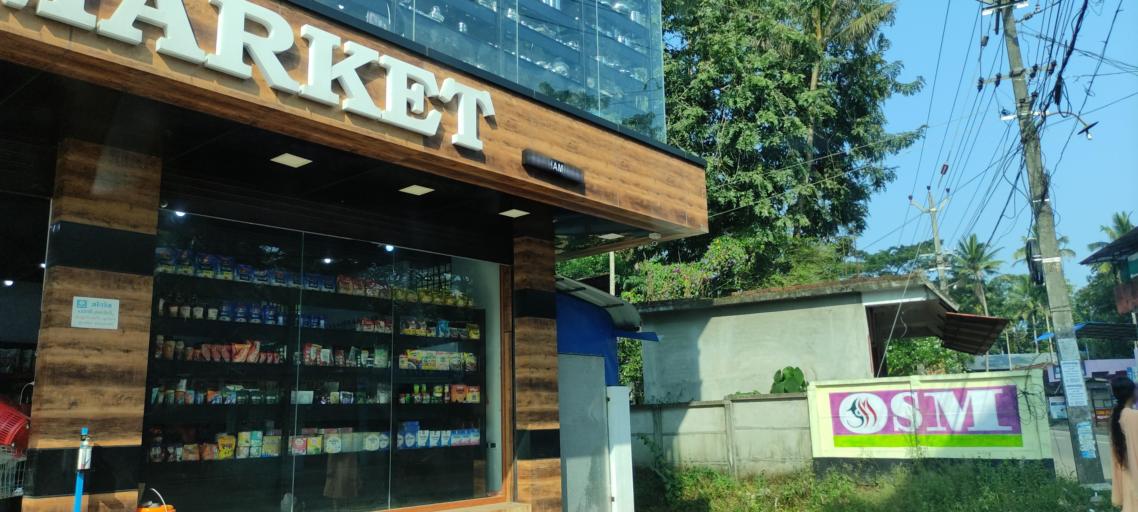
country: IN
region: Kerala
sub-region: Pattanamtitta
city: Adur
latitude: 9.0746
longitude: 76.6599
